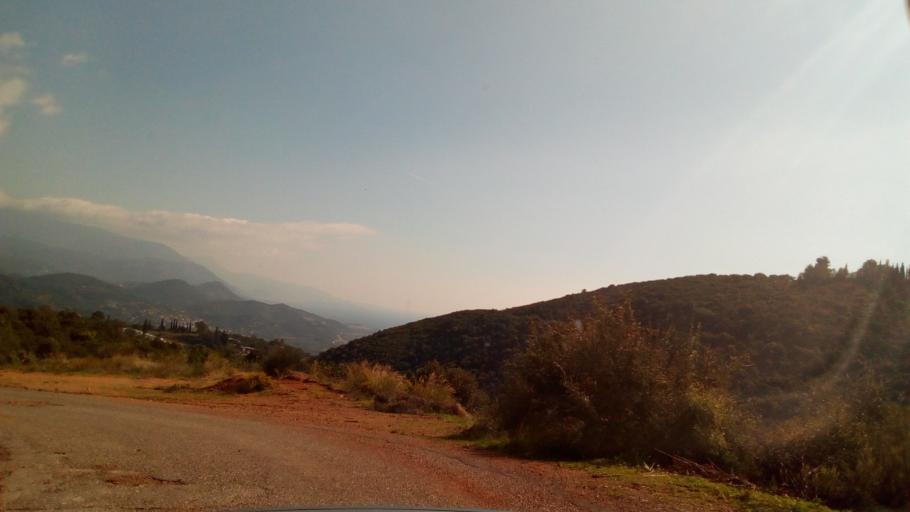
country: GR
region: West Greece
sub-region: Nomos Aitolias kai Akarnanias
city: Nafpaktos
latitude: 38.4209
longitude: 21.8524
